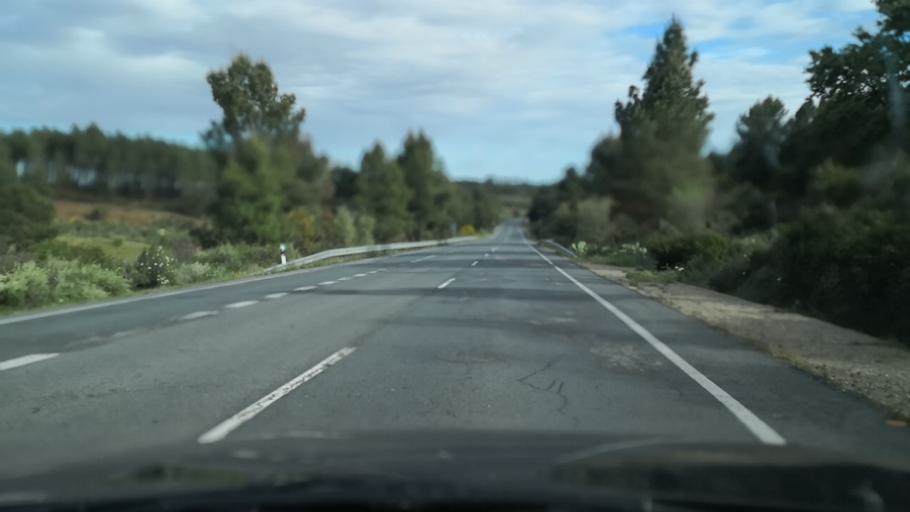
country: ES
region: Extremadura
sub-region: Provincia de Caceres
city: Perales del Puerto
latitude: 40.1507
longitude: -6.6781
